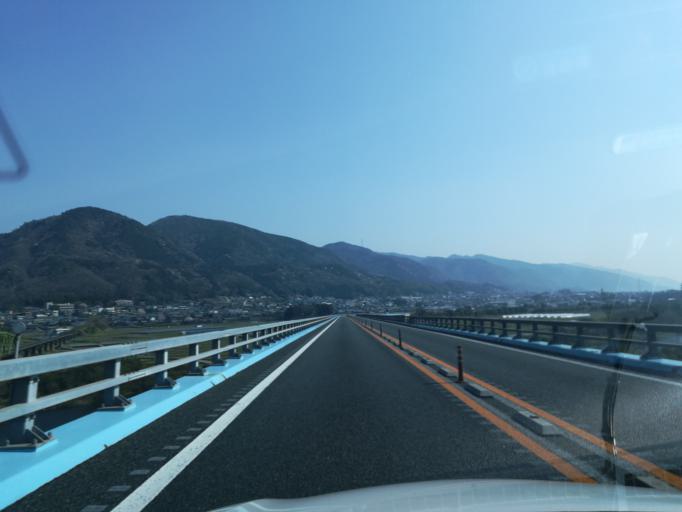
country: JP
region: Tokushima
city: Ikedacho
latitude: 34.0334
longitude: 133.8632
